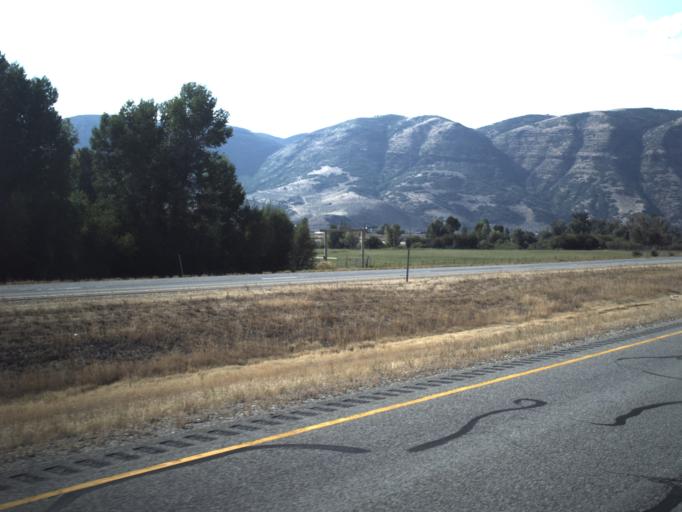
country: US
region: Utah
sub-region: Summit County
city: Coalville
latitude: 41.0289
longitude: -111.5006
